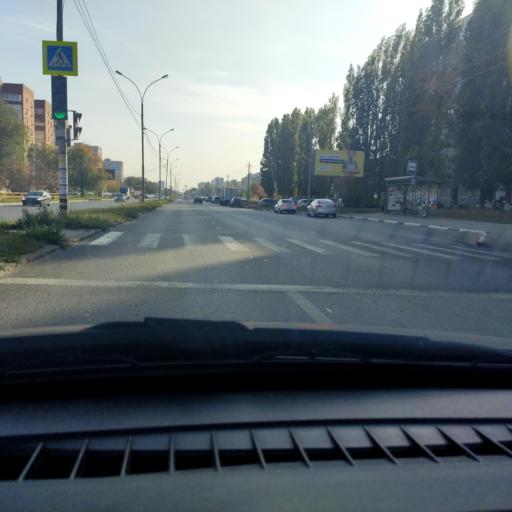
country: RU
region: Samara
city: Tol'yatti
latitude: 53.5399
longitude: 49.3152
